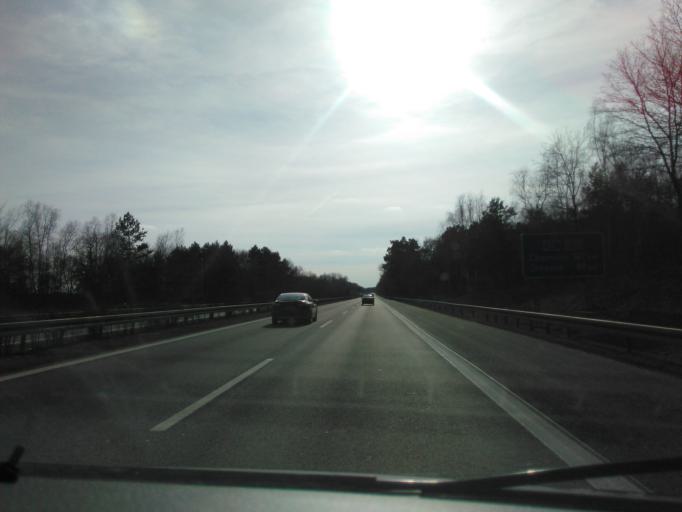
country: DE
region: Brandenburg
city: Lubbenau
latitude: 51.8251
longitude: 13.9051
